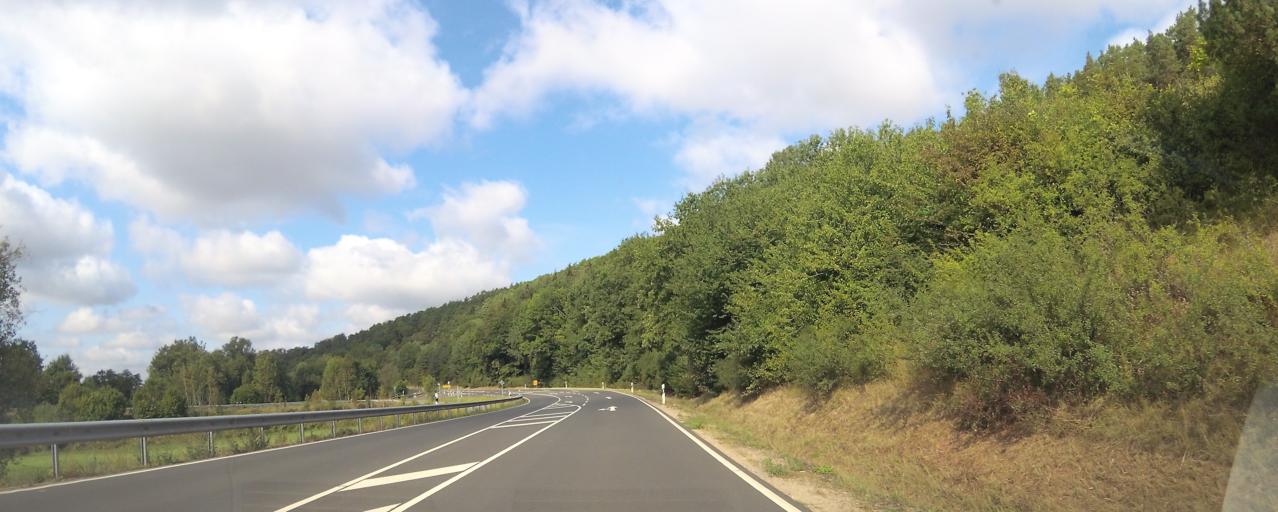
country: DE
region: Rheinland-Pfalz
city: Beilingen
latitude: 49.9675
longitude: 6.6641
